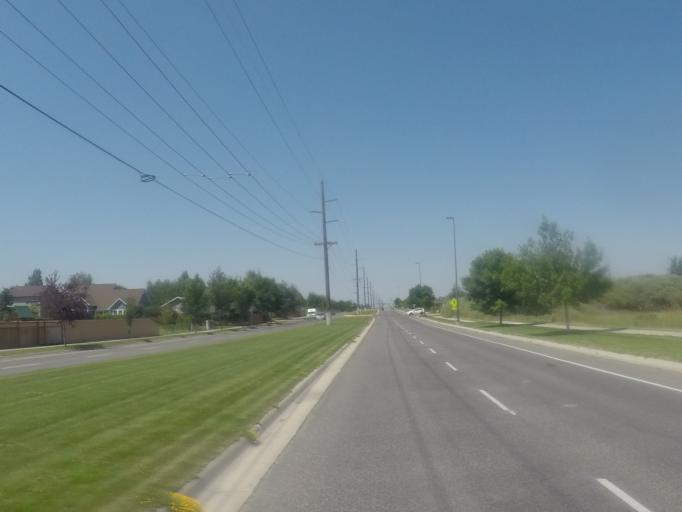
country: US
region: Montana
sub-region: Gallatin County
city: Bozeman
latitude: 45.6930
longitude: -111.0754
